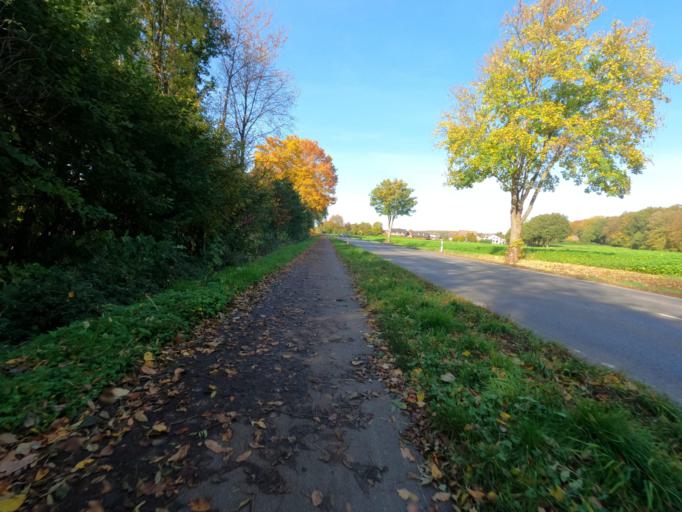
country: DE
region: North Rhine-Westphalia
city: Huckelhoven
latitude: 51.0422
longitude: 6.2536
